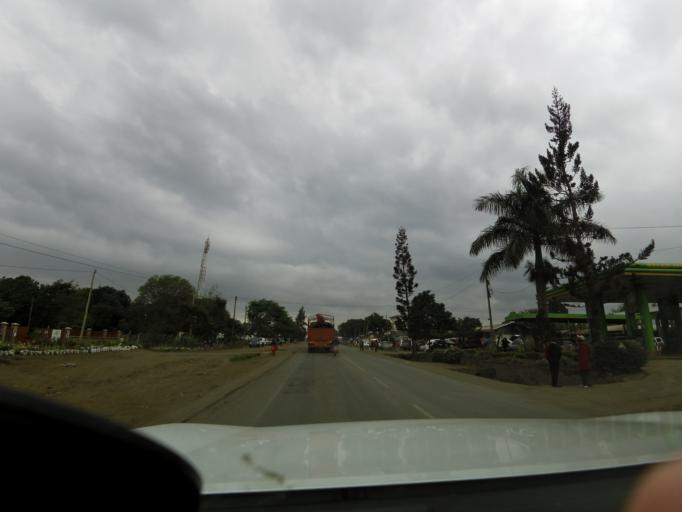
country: TZ
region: Arusha
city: Arusha
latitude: -3.3617
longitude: 36.6859
